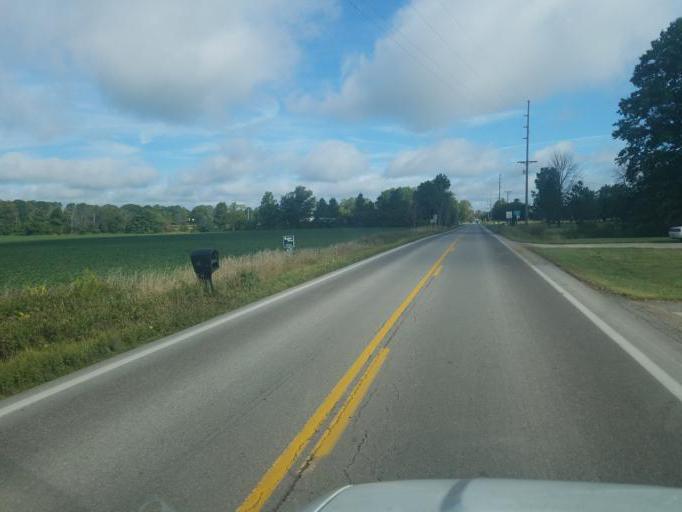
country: US
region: Ohio
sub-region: Wayne County
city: West Salem
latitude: 40.9795
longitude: -82.1098
